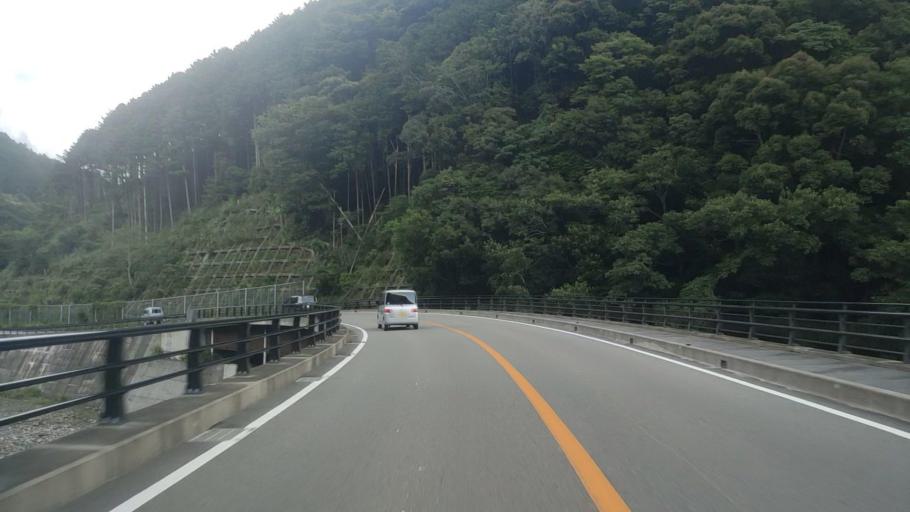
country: JP
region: Wakayama
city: Tanabe
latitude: 33.7720
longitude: 135.5005
